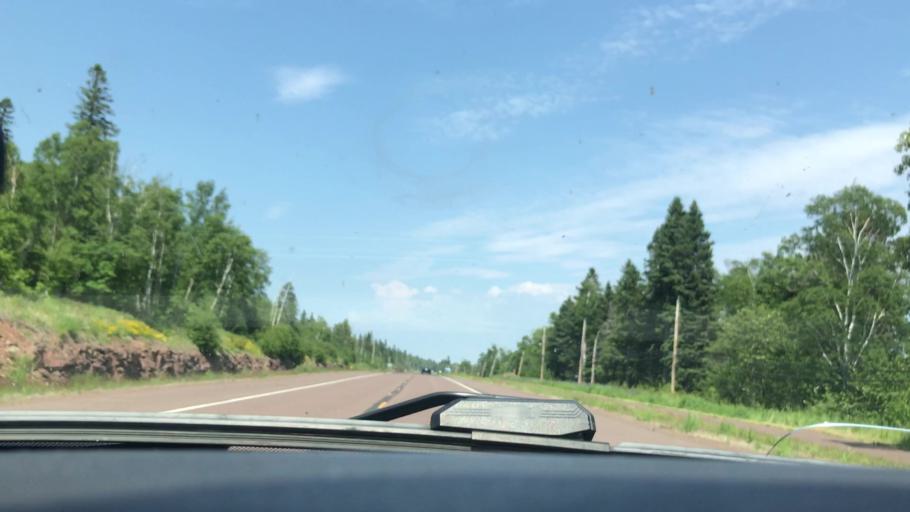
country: US
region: Minnesota
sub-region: Cook County
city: Grand Marais
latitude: 47.6113
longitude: -90.7638
